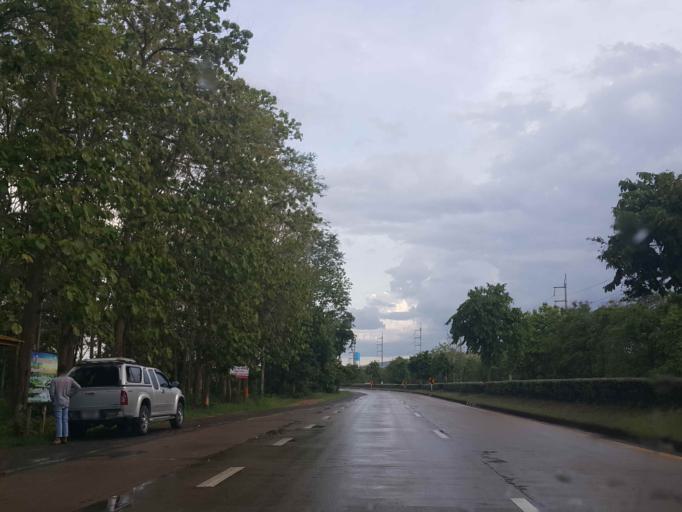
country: TH
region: Phrae
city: Den Chai
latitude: 17.9968
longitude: 100.1008
